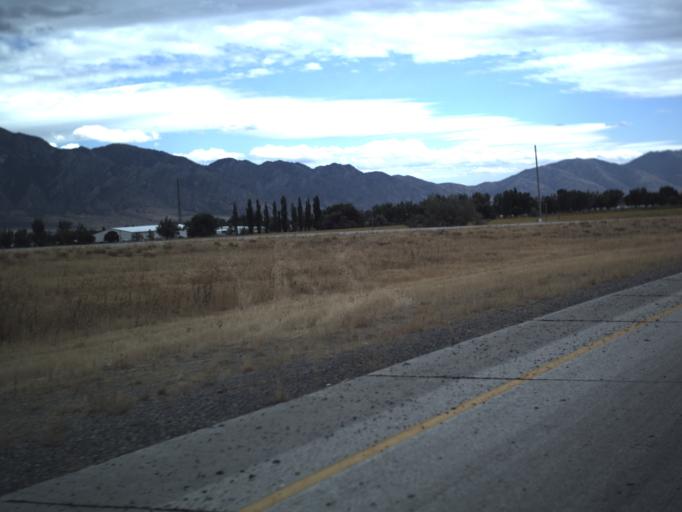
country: US
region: Utah
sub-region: Box Elder County
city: Tremonton
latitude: 41.7233
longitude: -112.1933
